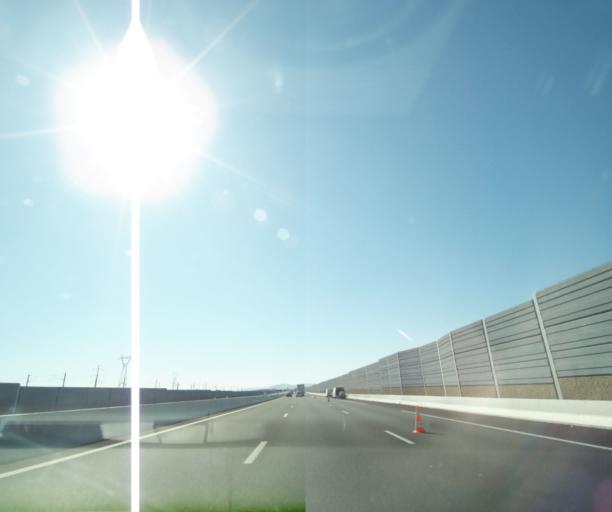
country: FR
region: Languedoc-Roussillon
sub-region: Departement de l'Herault
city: Lattes
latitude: 43.5862
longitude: 3.9024
